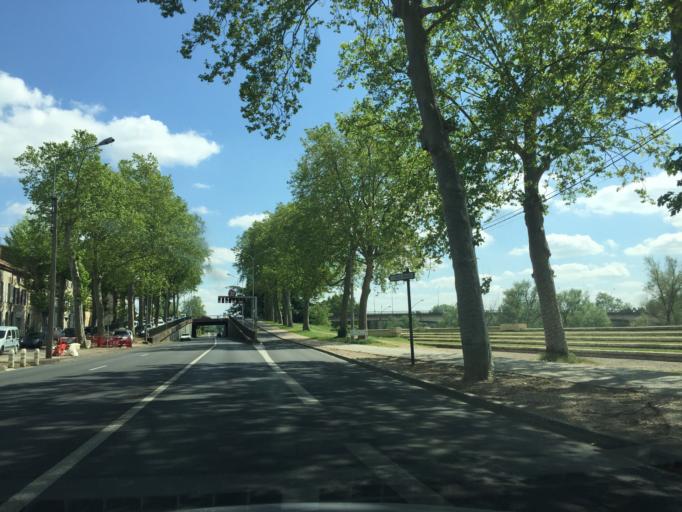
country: FR
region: Aquitaine
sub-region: Departement du Lot-et-Garonne
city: Le Passage
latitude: 44.1973
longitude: 0.6122
